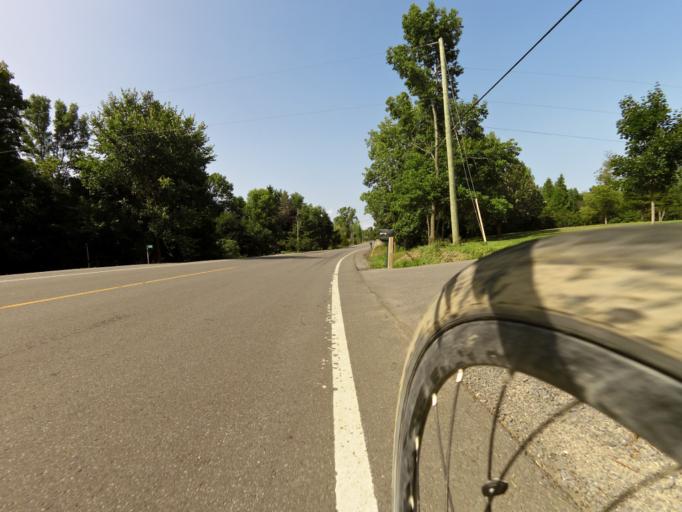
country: CA
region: Ontario
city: Skatepark
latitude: 44.2550
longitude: -76.7238
